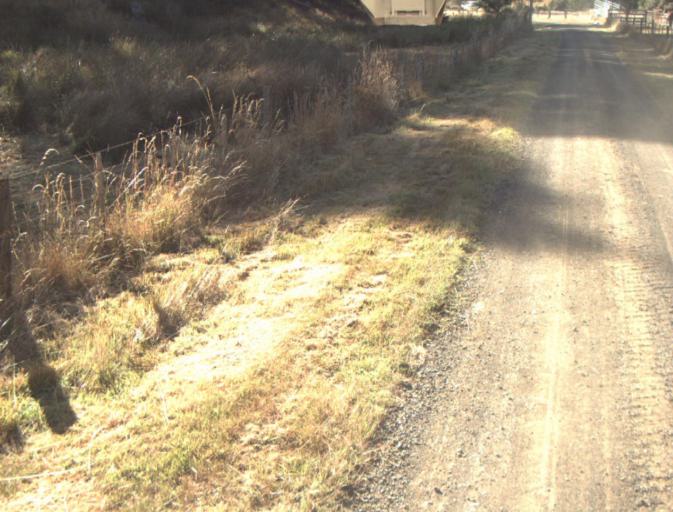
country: AU
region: Tasmania
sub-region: Launceston
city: Mayfield
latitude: -41.2867
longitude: 147.1907
